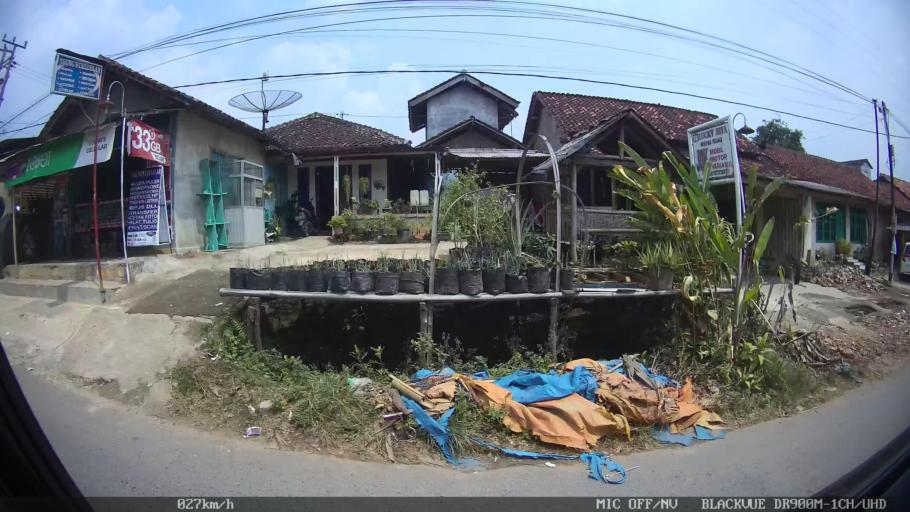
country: ID
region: Lampung
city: Gadingrejo
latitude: -5.3756
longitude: 105.0560
